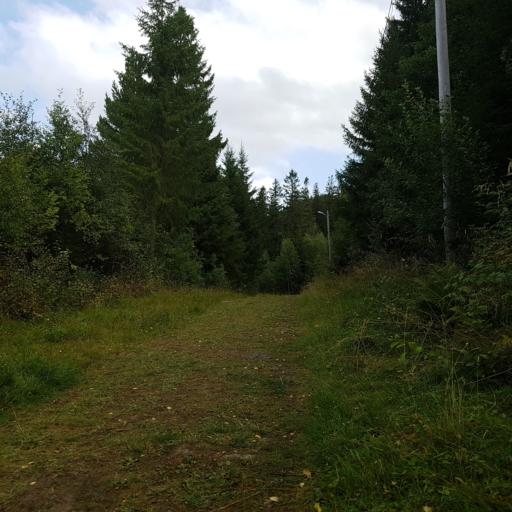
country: NO
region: Sor-Trondelag
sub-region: Skaun
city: Borsa
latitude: 63.4310
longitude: 10.1902
